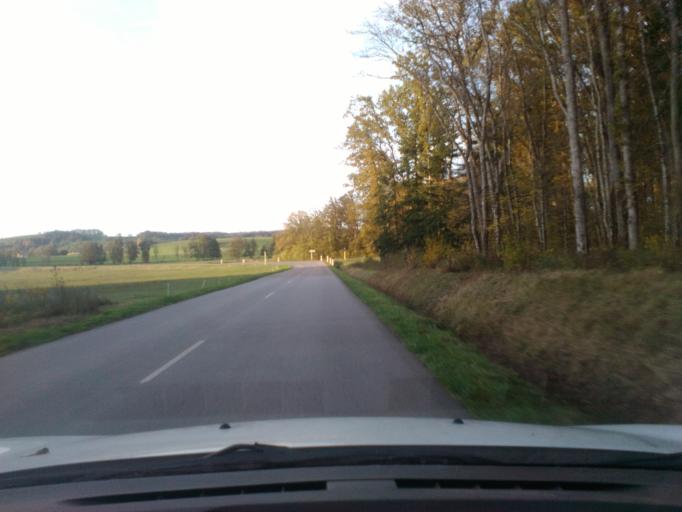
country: FR
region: Lorraine
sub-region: Departement des Vosges
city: Mirecourt
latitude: 48.2491
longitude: 6.2032
